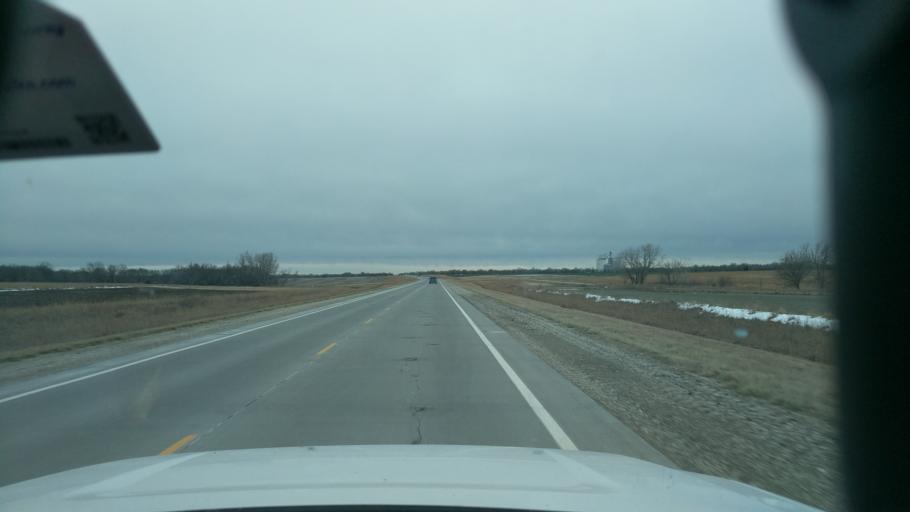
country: US
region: Kansas
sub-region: Dickinson County
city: Herington
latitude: 38.5113
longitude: -96.9569
